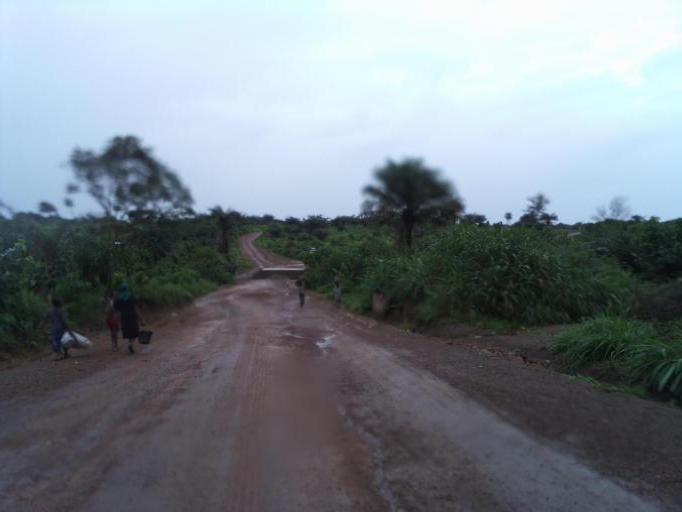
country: SL
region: Eastern Province
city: Kenema
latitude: 7.8752
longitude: -11.1517
